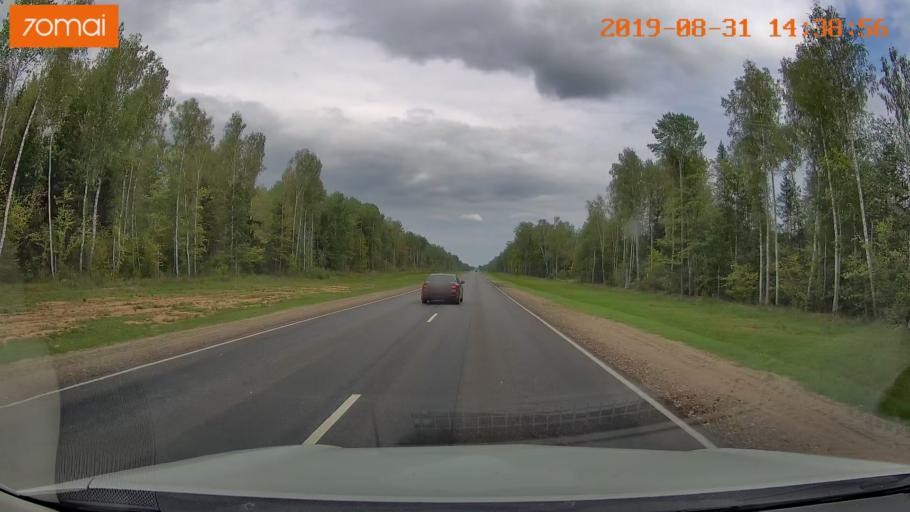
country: RU
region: Smolensk
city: Yekimovichi
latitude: 54.1880
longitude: 33.5405
